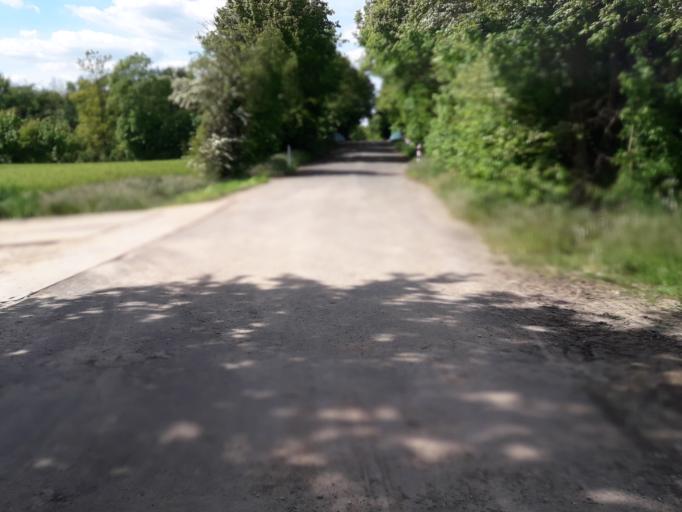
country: DE
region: North Rhine-Westphalia
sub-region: Regierungsbezirk Detmold
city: Paderborn
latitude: 51.7033
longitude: 8.7868
